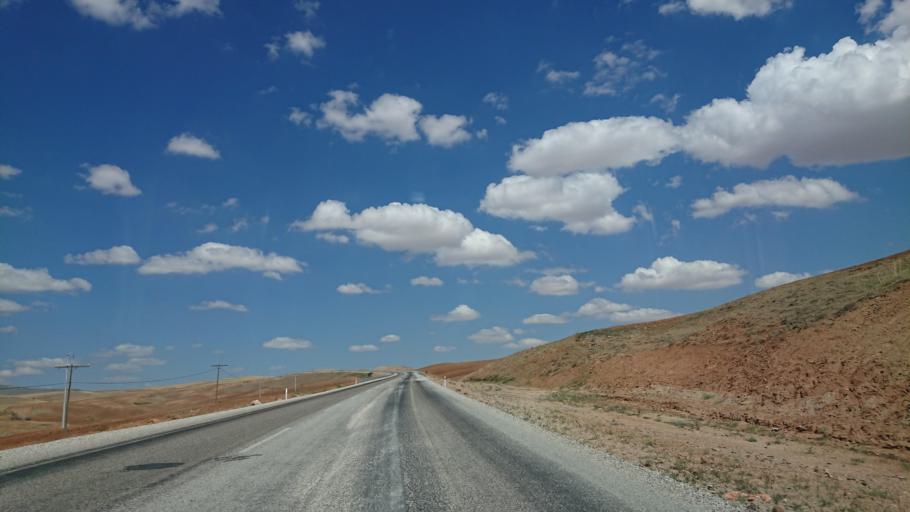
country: TR
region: Ankara
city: Evren
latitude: 39.1068
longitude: 33.9160
